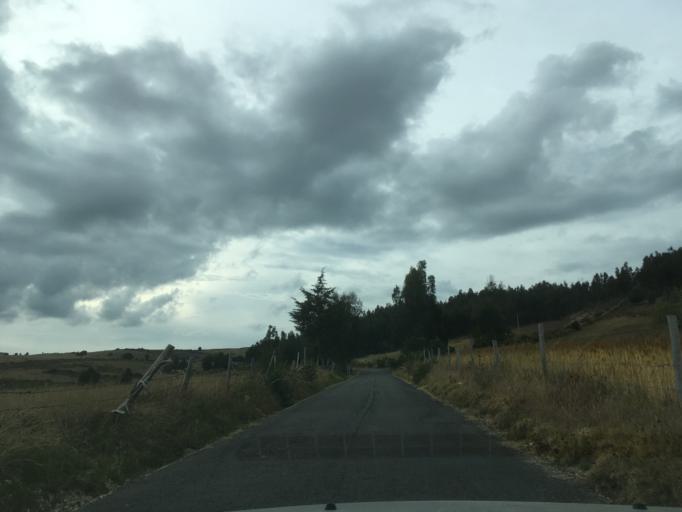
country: CO
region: Boyaca
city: Firavitoba
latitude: 5.6795
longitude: -73.0235
